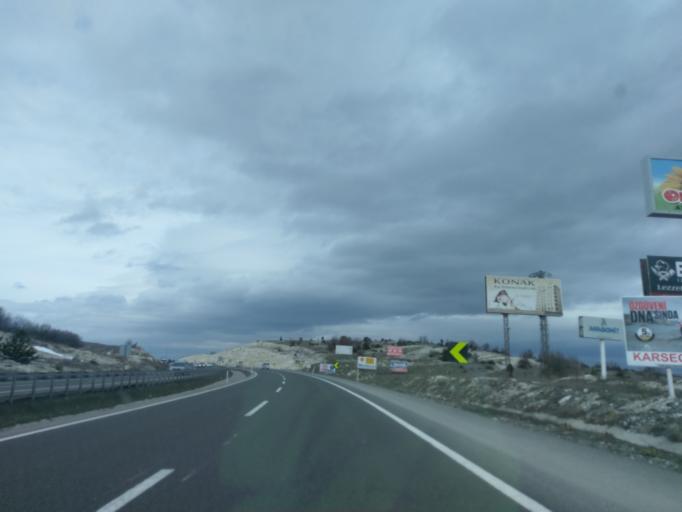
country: TR
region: Kuetahya
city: Kutahya
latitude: 39.3735
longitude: 30.0653
